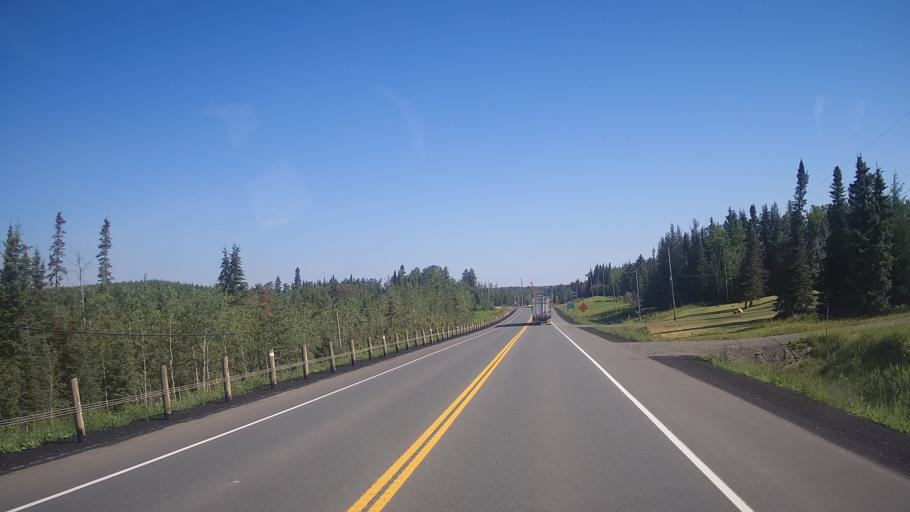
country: CA
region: Ontario
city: Dryden
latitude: 49.6799
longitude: -92.4926
